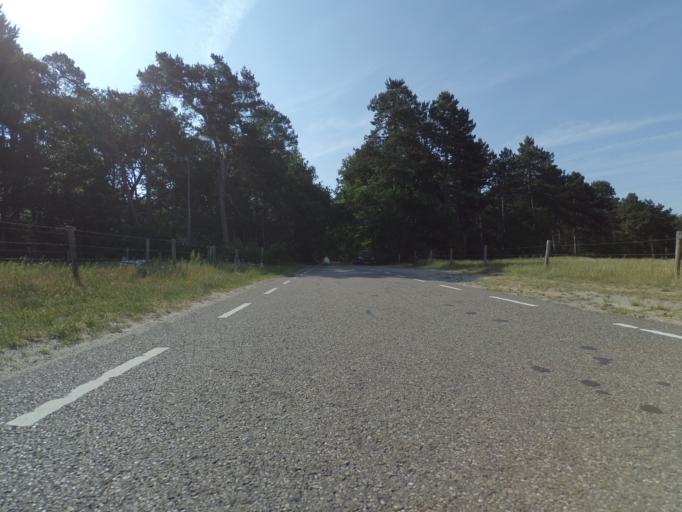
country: NL
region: North Brabant
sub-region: Gemeente Bergen op Zoom
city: Bergen op Zoom
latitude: 51.4815
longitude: 4.3308
